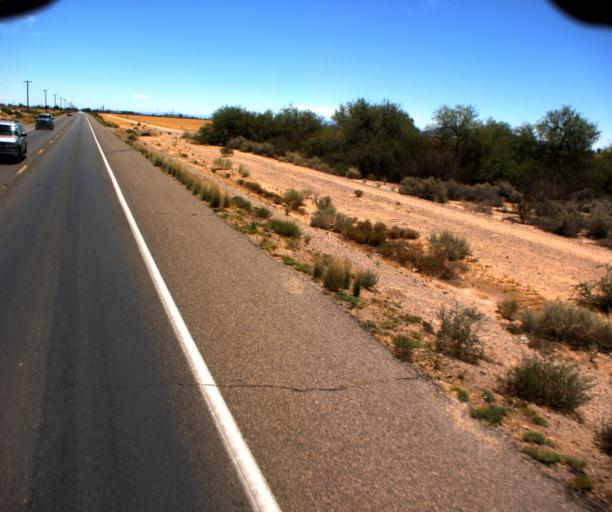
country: US
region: Arizona
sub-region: Pinal County
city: Casa Grande
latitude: 32.8794
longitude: -111.8184
